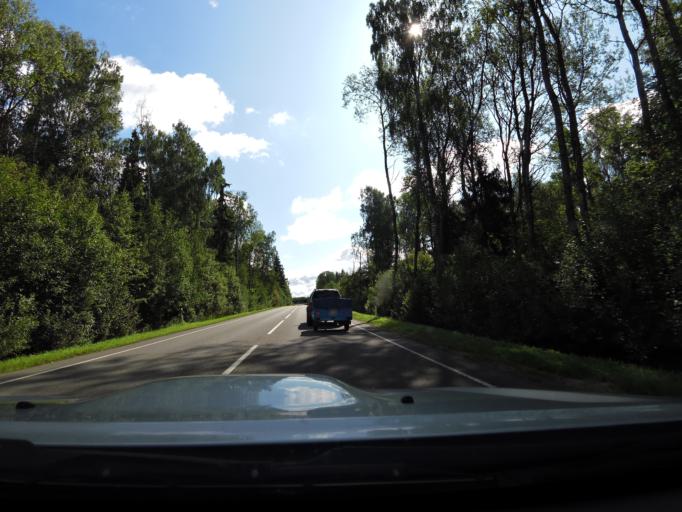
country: LT
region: Utenos apskritis
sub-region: Utena
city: Utena
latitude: 55.4870
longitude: 25.6327
